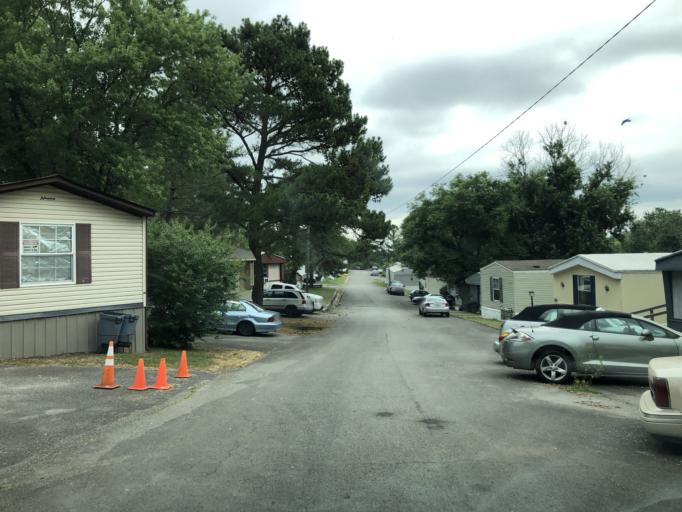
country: US
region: Tennessee
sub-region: Davidson County
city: Goodlettsville
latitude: 36.2925
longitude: -86.7448
